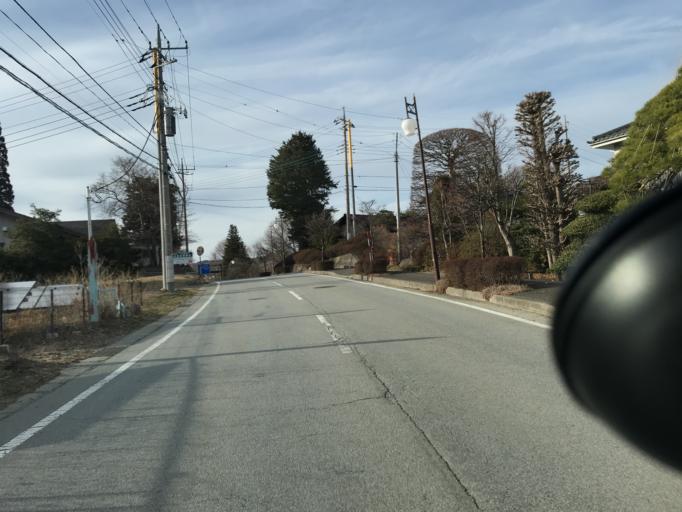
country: JP
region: Nagano
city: Chino
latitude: 35.8665
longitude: 138.3004
